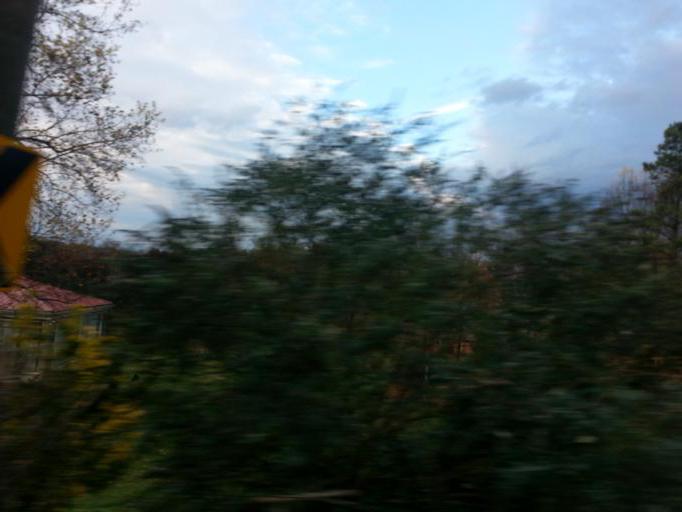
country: US
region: Tennessee
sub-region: Knox County
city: Knoxville
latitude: 35.9297
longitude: -84.0162
